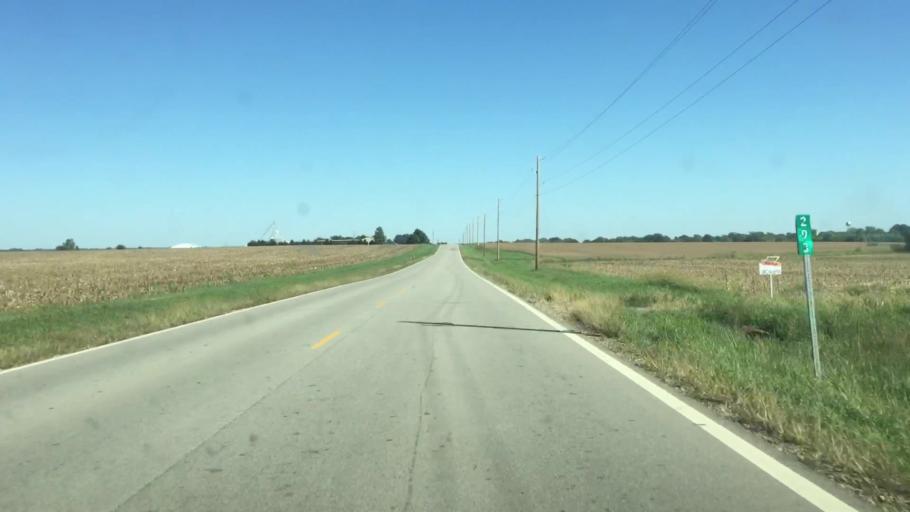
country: US
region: Kansas
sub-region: Brown County
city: Horton
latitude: 39.5949
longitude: -95.6300
